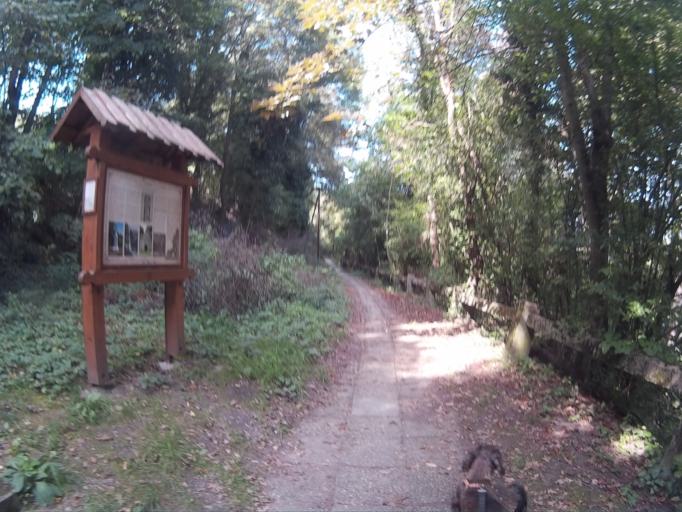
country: HU
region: Vas
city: Koszeg
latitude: 47.3975
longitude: 16.5354
